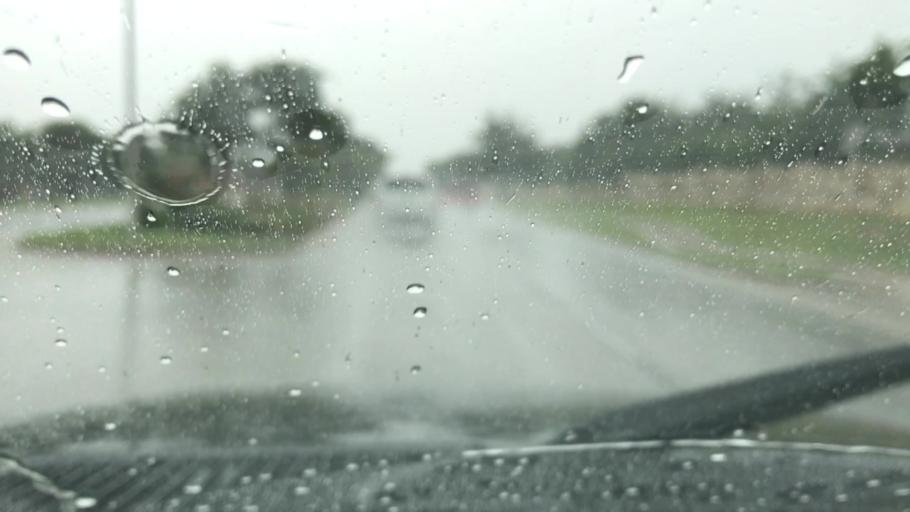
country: US
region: Texas
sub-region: Williamson County
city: Leander
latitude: 30.5342
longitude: -97.8601
